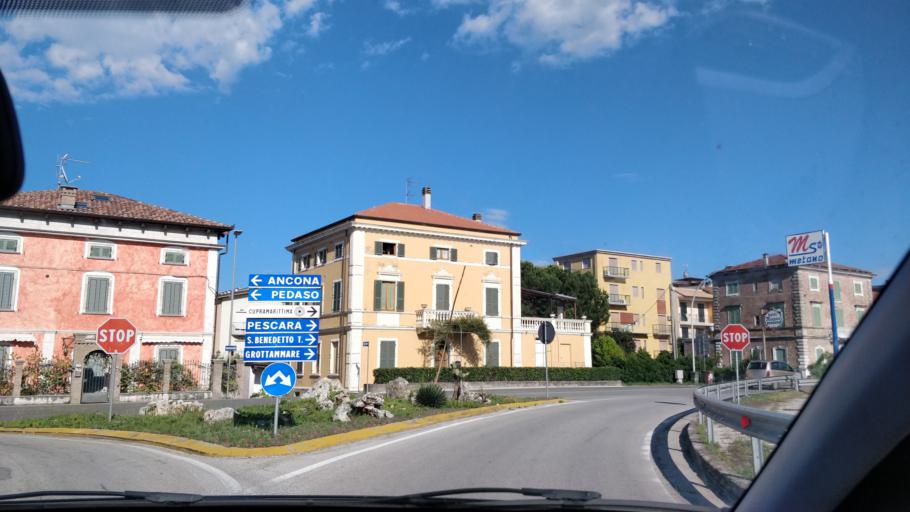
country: IT
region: The Marches
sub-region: Provincia di Ascoli Piceno
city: Cupra Marittima
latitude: 43.0352
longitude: 13.8557
